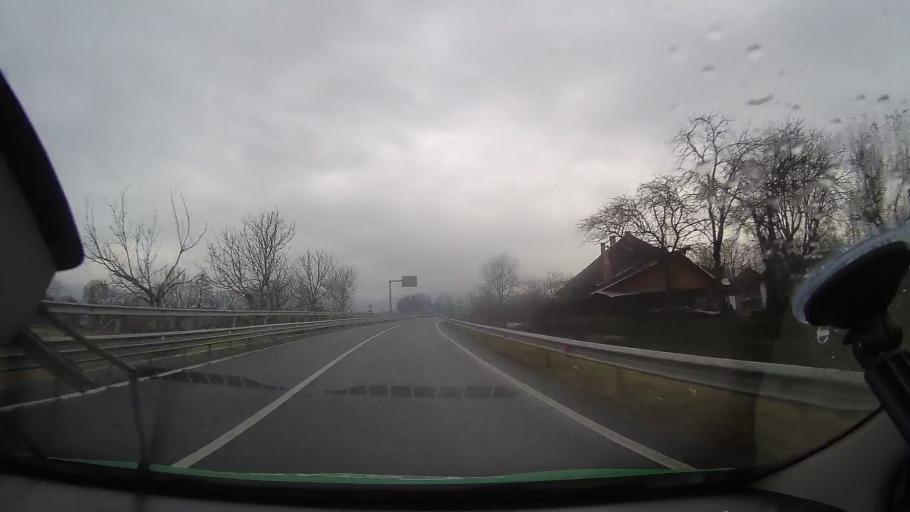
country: RO
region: Hunedoara
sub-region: Comuna Baia de Cris
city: Baia de Cris
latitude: 46.1699
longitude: 22.7272
